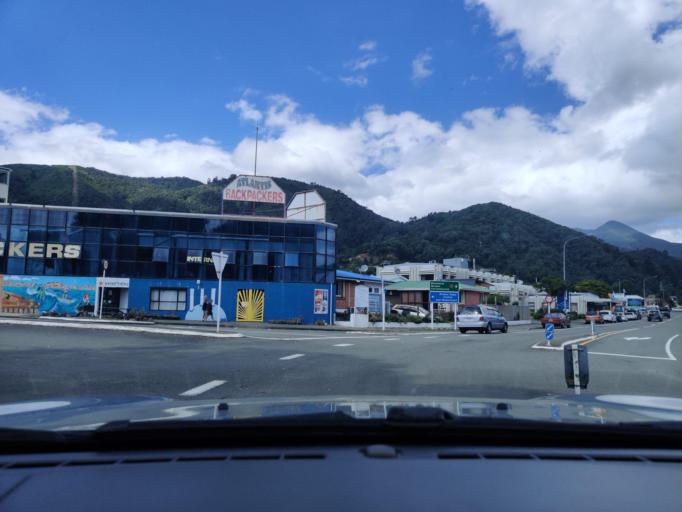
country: NZ
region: Marlborough
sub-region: Marlborough District
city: Picton
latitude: -41.2888
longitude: 174.0055
